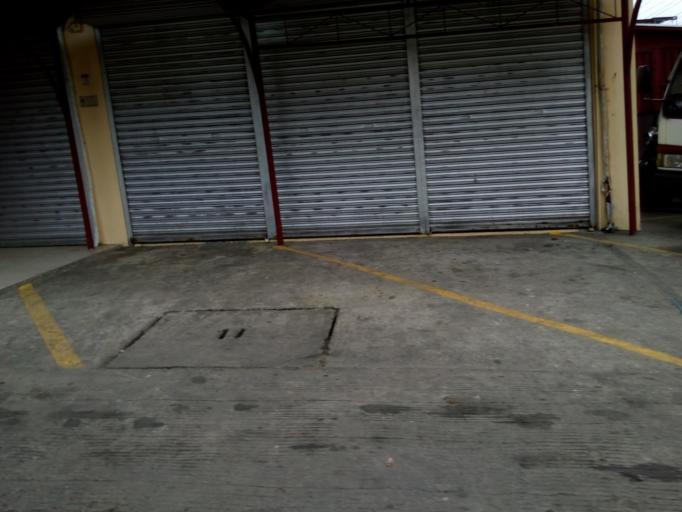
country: PH
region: Caraga
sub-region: Province of Surigao del Norte
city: Surigao
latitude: 9.7872
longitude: 125.4916
